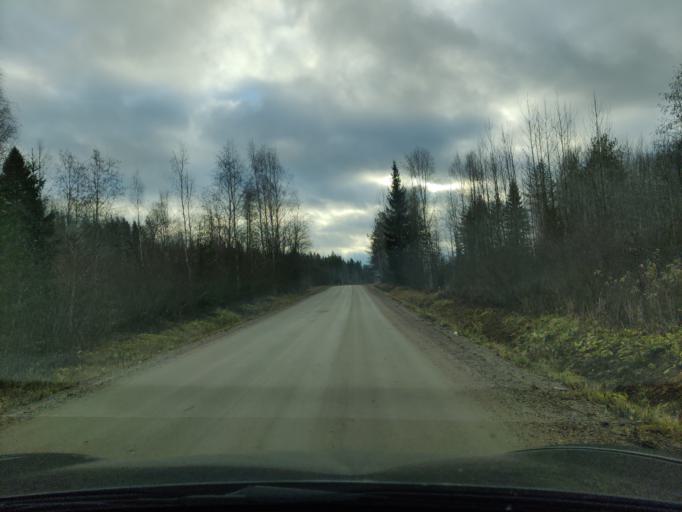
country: FI
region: Northern Savo
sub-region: Ylae-Savo
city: Kiuruvesi
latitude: 63.6392
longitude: 26.6339
